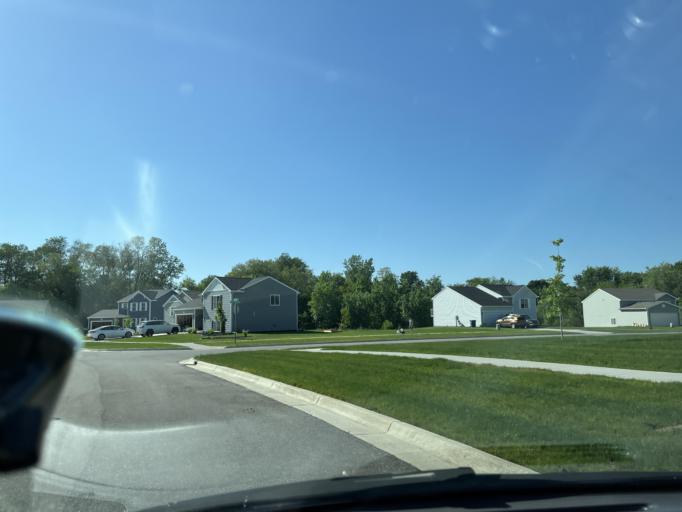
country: US
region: Michigan
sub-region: Barry County
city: Middleville
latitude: 42.7058
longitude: -85.4797
